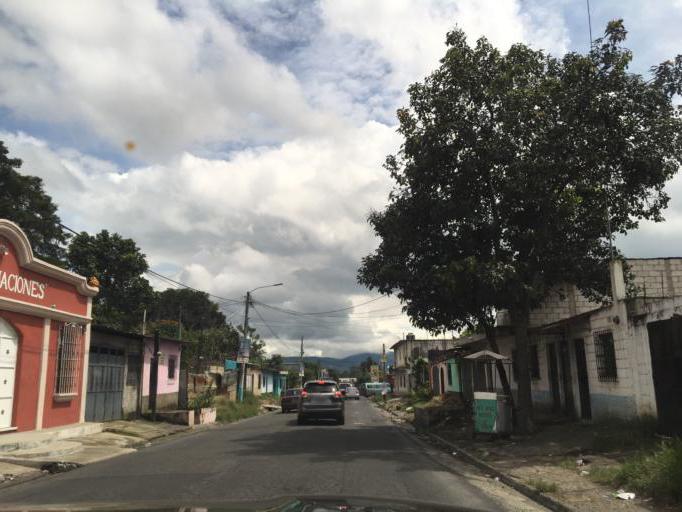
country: GT
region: Guatemala
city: Villa Nueva
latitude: 14.5071
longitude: -90.5855
